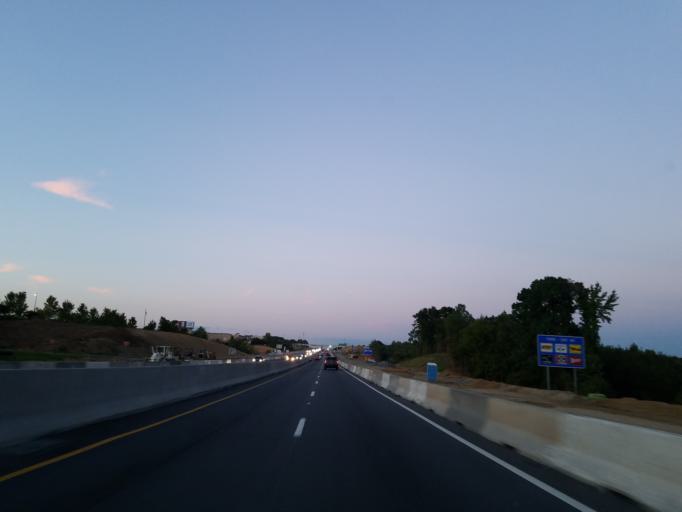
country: US
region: North Carolina
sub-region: Cabarrus County
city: Kannapolis
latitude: 35.4578
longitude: -80.5921
